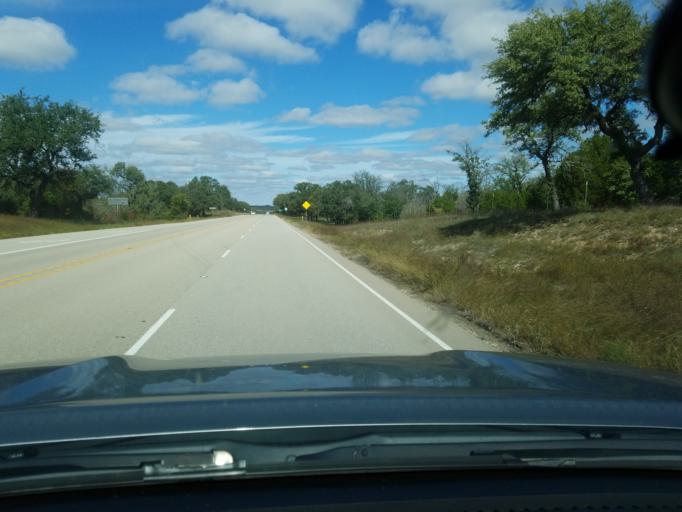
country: US
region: Texas
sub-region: Hamilton County
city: Hamilton
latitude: 31.5939
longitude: -98.1571
